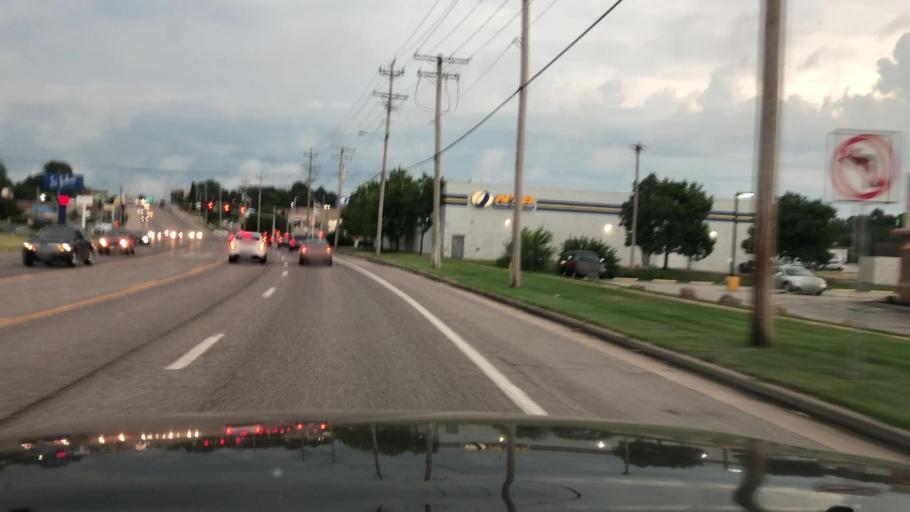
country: US
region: Missouri
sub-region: Saint Louis County
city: Bridgeton
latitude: 38.7474
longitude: -90.4220
